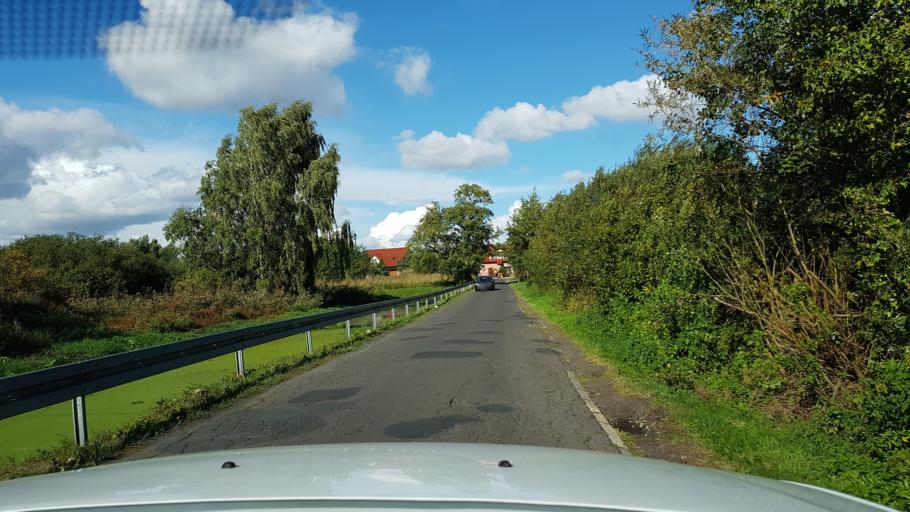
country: PL
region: West Pomeranian Voivodeship
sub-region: Powiat gryfinski
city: Gryfino
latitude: 53.2748
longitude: 14.4938
